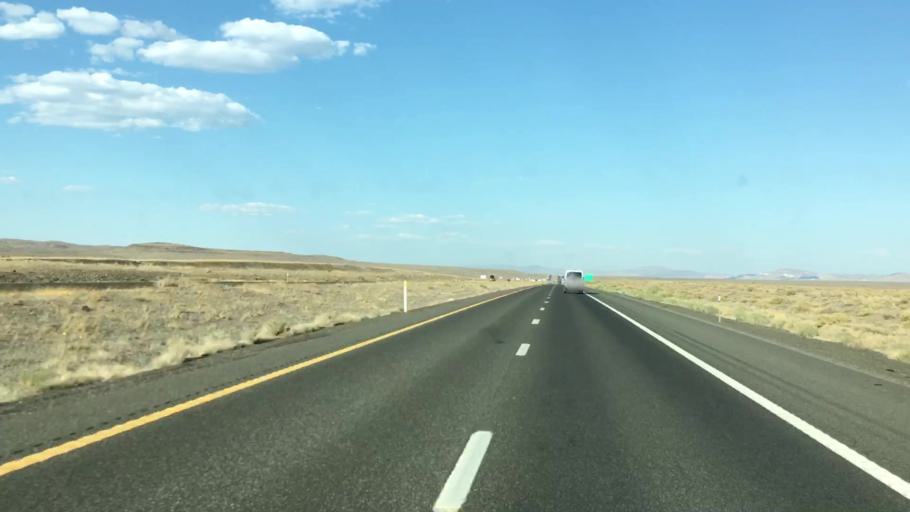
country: US
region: Nevada
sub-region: Pershing County
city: Lovelock
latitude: 39.9366
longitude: -118.7629
